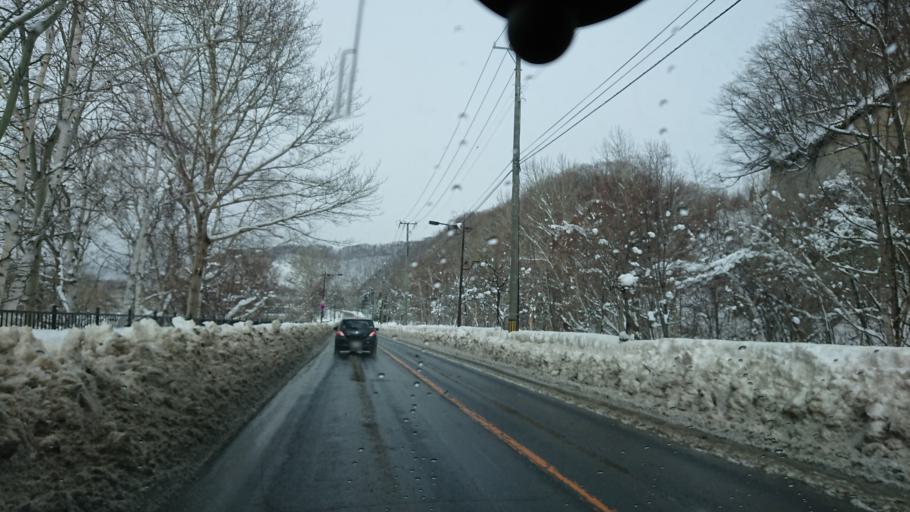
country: JP
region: Hokkaido
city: Sapporo
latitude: 42.9776
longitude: 141.3443
